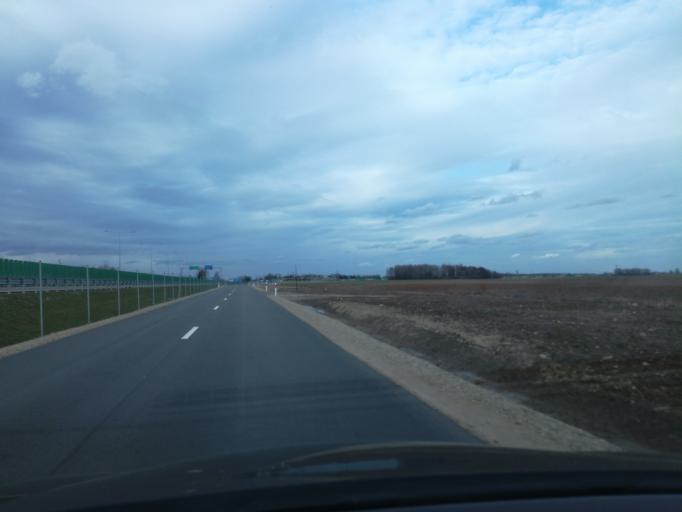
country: LT
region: Marijampoles apskritis
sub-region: Marijampole Municipality
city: Marijampole
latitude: 54.6219
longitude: 23.4192
